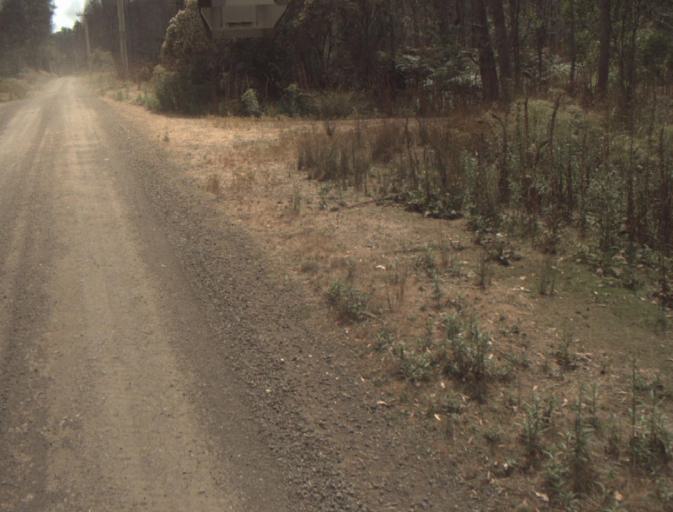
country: AU
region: Tasmania
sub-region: Launceston
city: Mayfield
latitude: -41.1976
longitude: 147.2626
